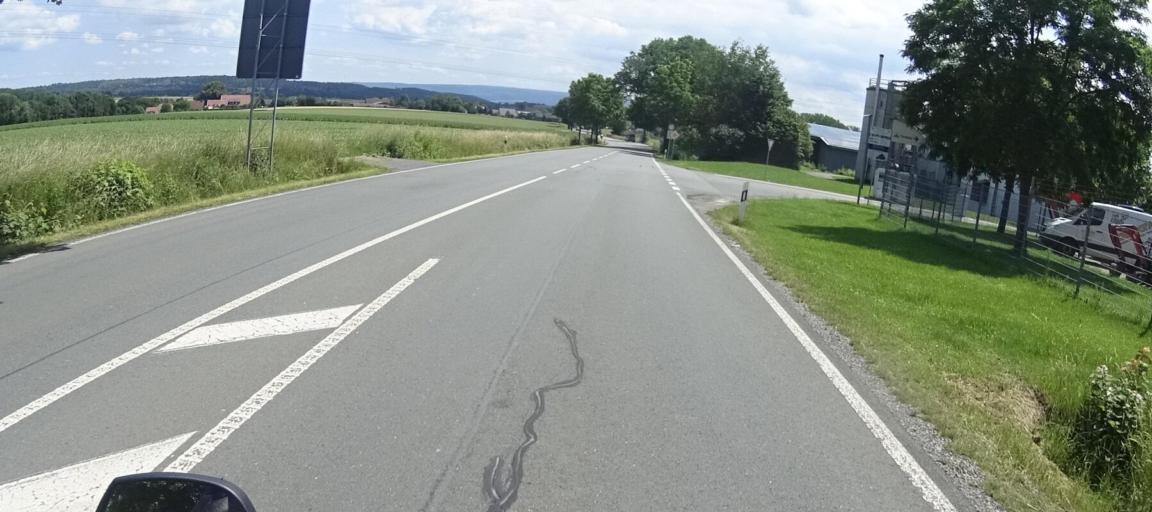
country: DE
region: Lower Saxony
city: Vahlbruch
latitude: 51.8334
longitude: 9.3080
